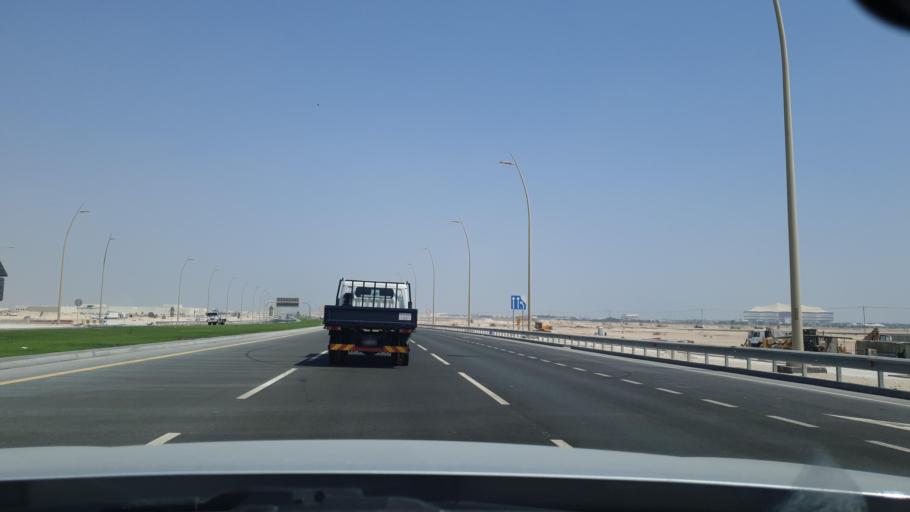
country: QA
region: Al Khawr
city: Al Khawr
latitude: 25.6524
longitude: 51.4567
